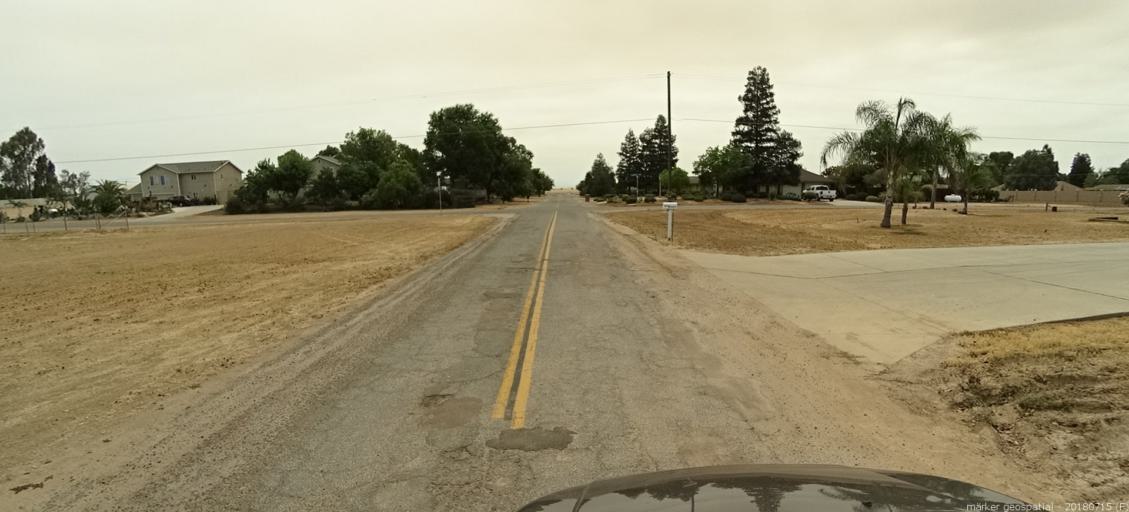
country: US
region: California
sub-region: Madera County
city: Madera Acres
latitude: 37.0142
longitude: -120.0599
